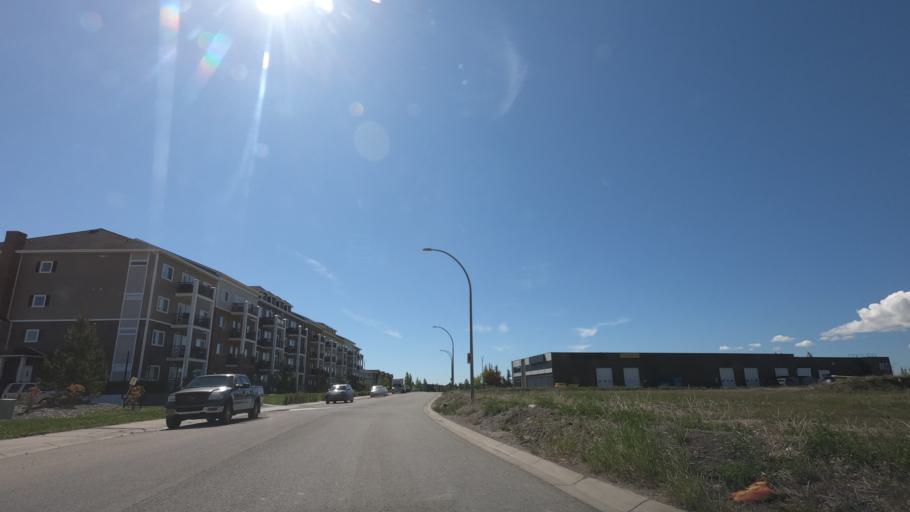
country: CA
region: Alberta
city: Airdrie
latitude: 51.2671
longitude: -113.9950
